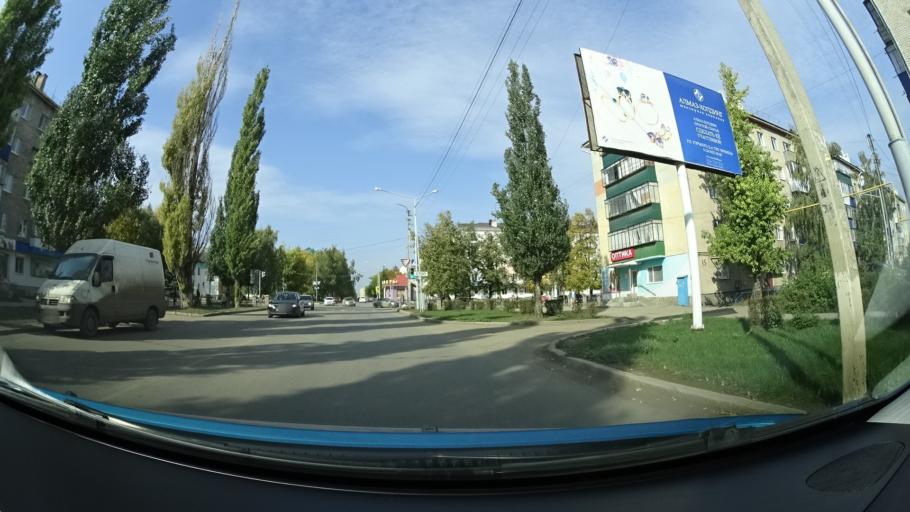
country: RU
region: Bashkortostan
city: Tuymazy
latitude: 54.6023
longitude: 53.7010
